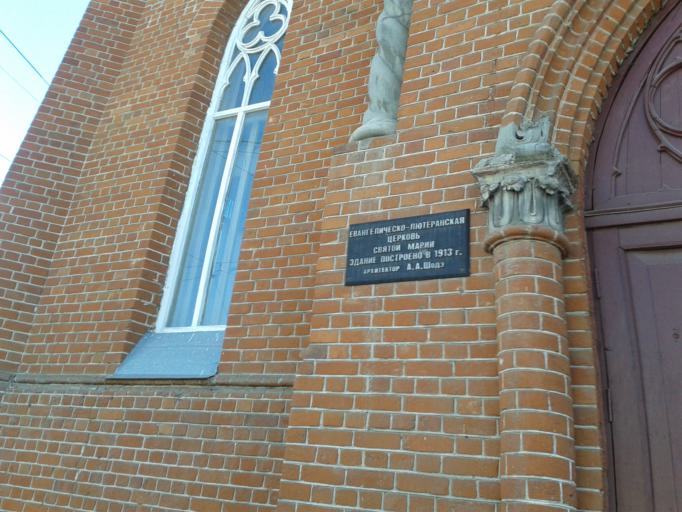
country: RU
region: Ulyanovsk
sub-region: Ulyanovskiy Rayon
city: Ulyanovsk
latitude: 54.3129
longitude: 48.3874
